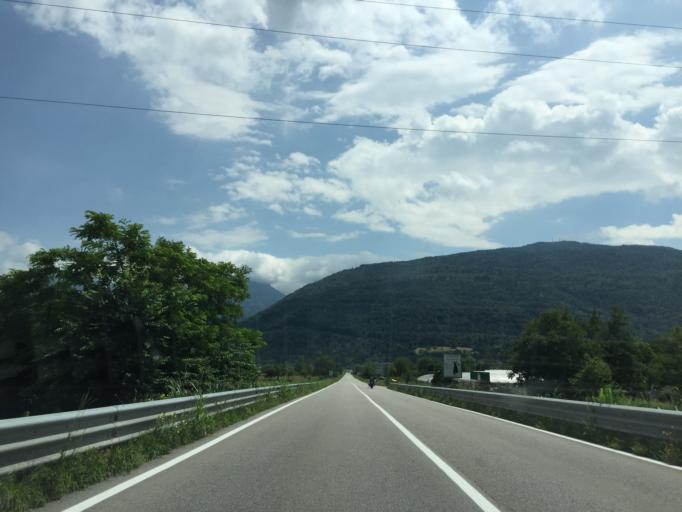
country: IT
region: Veneto
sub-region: Provincia di Belluno
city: Fonzaso
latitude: 46.0105
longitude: 11.7956
